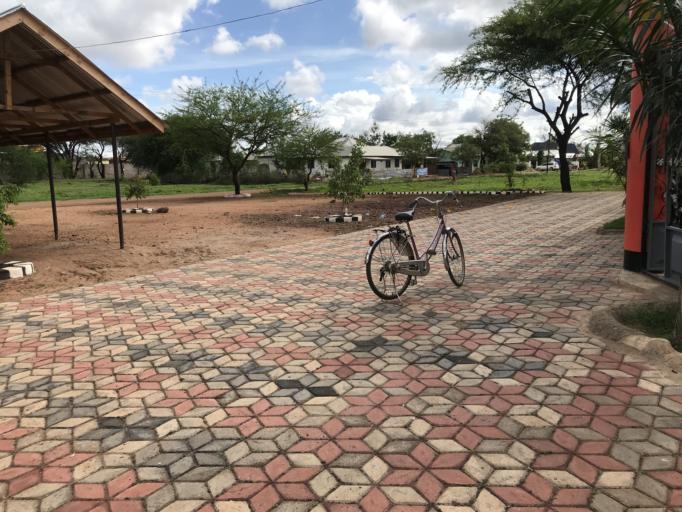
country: TZ
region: Tabora
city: Igunga
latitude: -4.2881
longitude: 33.8832
